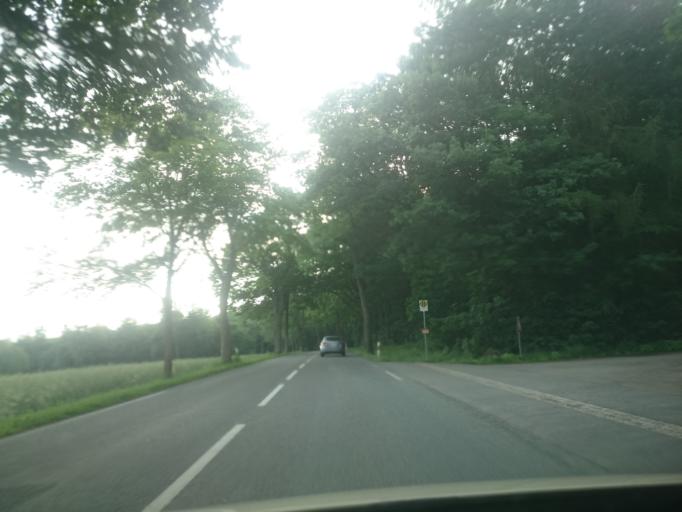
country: DE
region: Saxony
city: Bornichen
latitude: 50.7310
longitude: 13.1288
